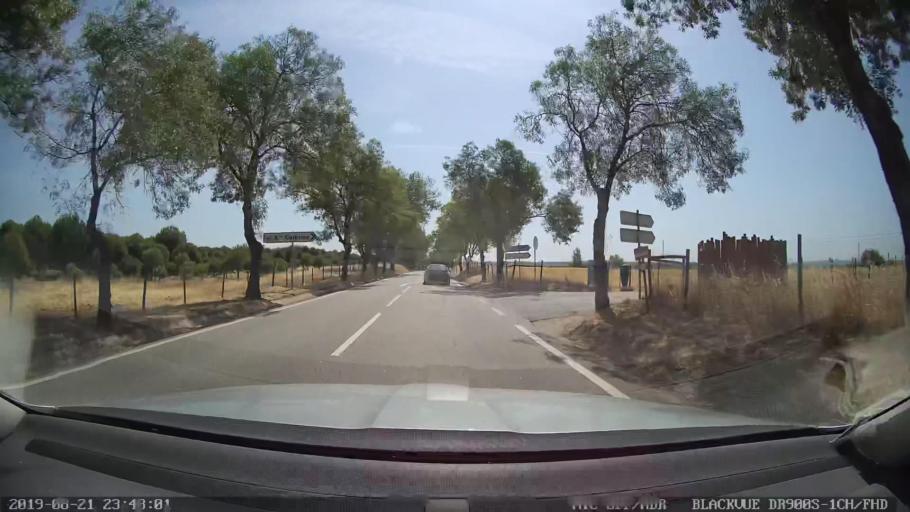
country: PT
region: Castelo Branco
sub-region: Idanha-A-Nova
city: Idanha-a-Nova
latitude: 39.8521
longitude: -7.3027
